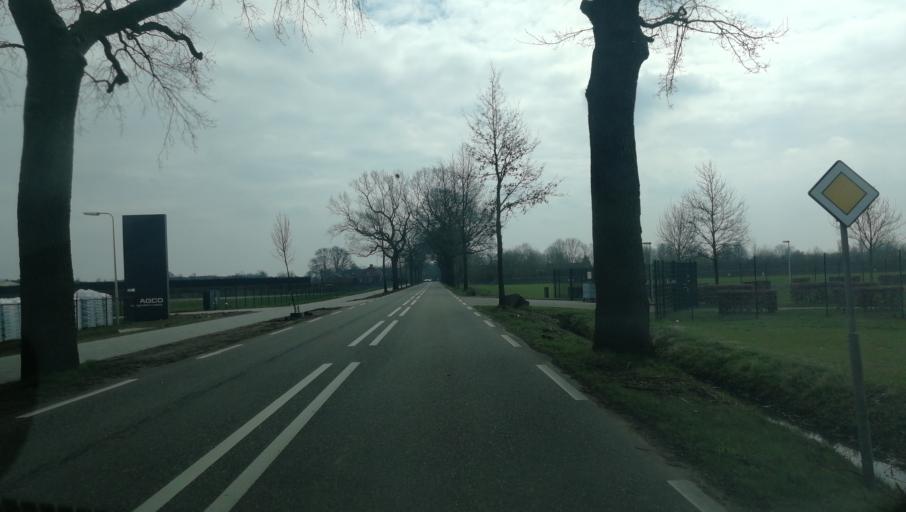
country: NL
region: Limburg
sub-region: Gemeente Venlo
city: Venlo
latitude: 51.4234
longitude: 6.1036
